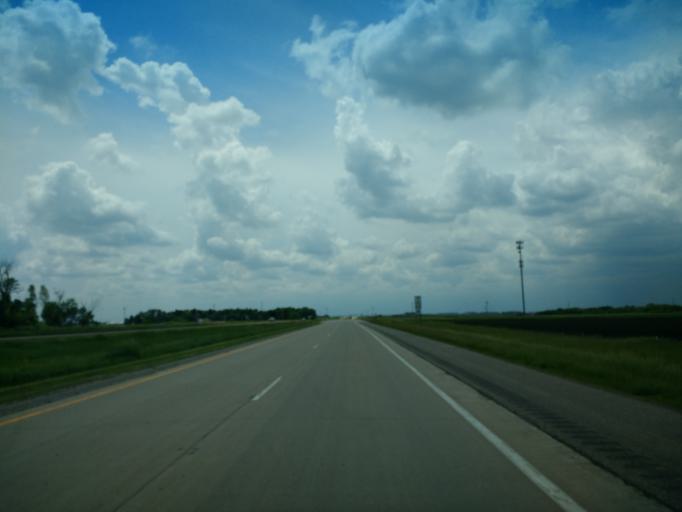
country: US
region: Minnesota
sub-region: Jackson County
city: Lakefield
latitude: 43.7657
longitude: -95.3688
